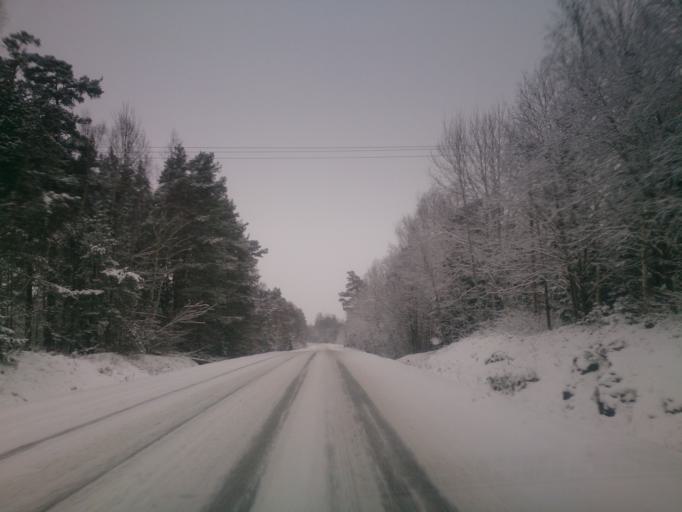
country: SE
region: OEstergoetland
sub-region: Finspangs Kommun
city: Finspang
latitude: 58.6245
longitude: 15.8196
